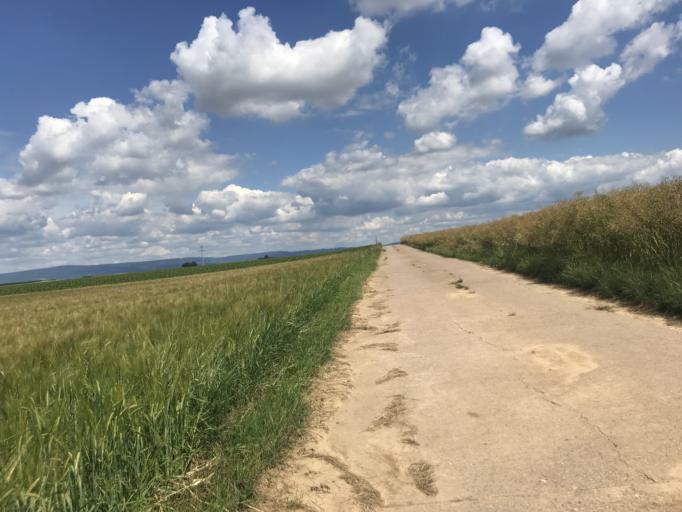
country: DE
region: Rheinland-Pfalz
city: Essenheim
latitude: 49.9402
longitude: 8.1404
